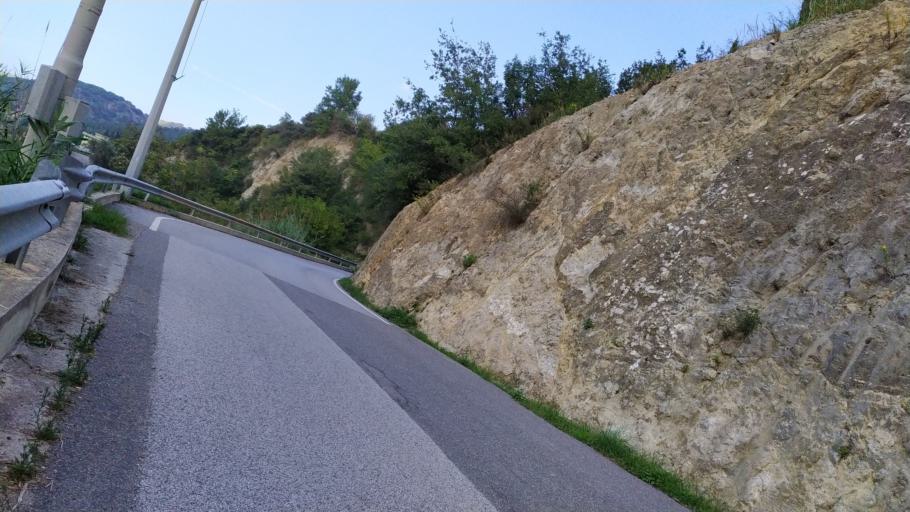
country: IT
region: Sicily
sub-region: Messina
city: Saponara
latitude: 38.1923
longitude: 15.4284
